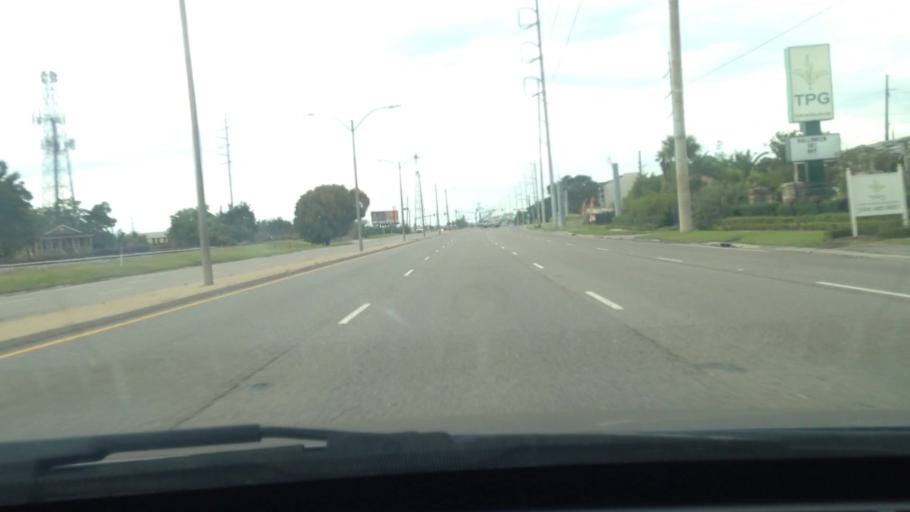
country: US
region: Louisiana
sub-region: Jefferson Parish
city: Jefferson
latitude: 29.9720
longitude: -90.1235
